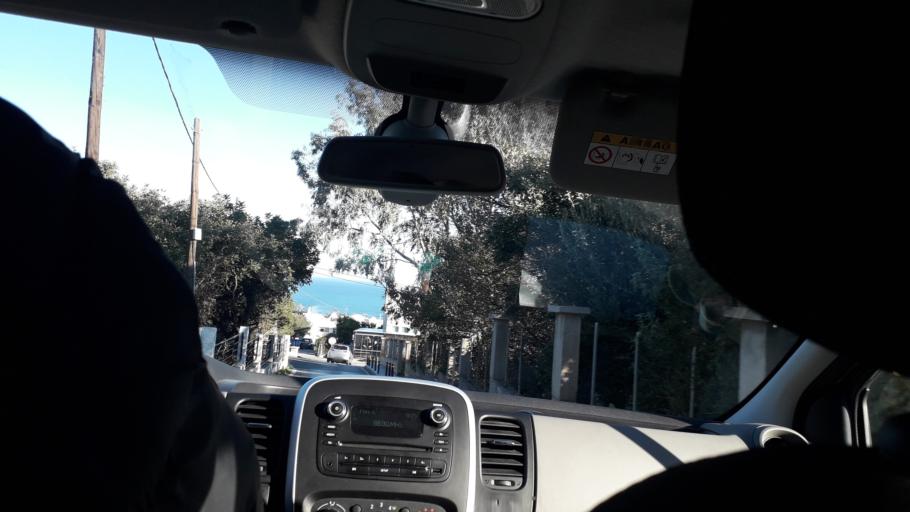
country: GR
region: Crete
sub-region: Nomos Rethymnis
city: Atsipopoulon
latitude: 35.3610
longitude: 24.4422
